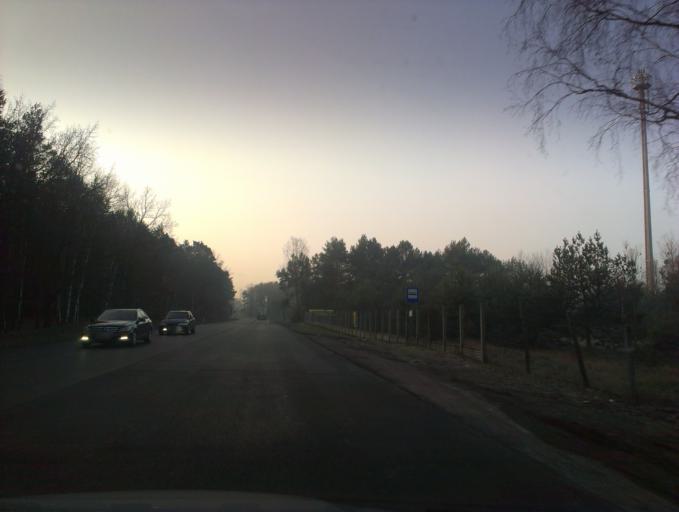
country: PL
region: Greater Poland Voivodeship
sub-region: Powiat obornicki
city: Oborniki
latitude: 52.7037
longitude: 16.8960
